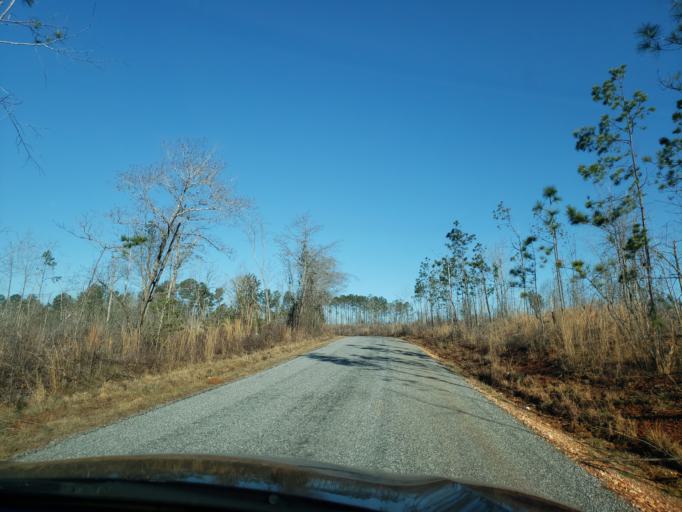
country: US
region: Alabama
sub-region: Elmore County
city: Tallassee
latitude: 32.6658
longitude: -85.8707
